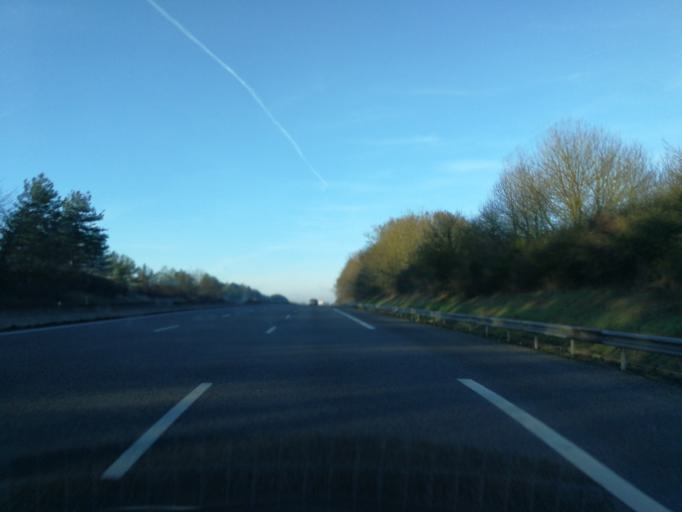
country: FR
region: Centre
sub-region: Departement d'Eure-et-Loir
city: Gallardon
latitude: 48.4929
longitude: 1.6763
